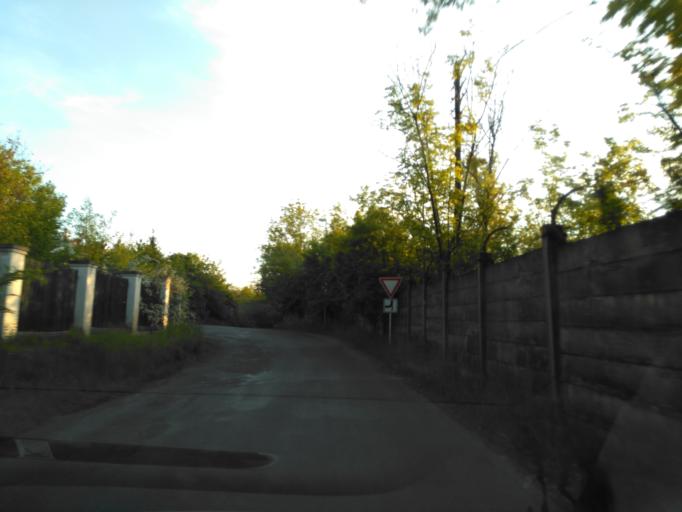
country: CZ
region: Central Bohemia
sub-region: Okres Beroun
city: Kraluv Dvur
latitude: 49.9394
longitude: 14.0378
